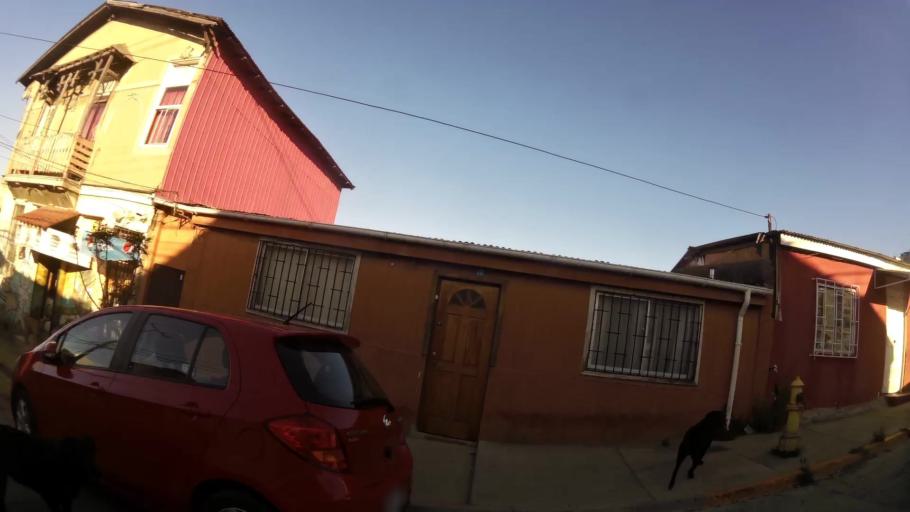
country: CL
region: Valparaiso
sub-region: Provincia de Valparaiso
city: Valparaiso
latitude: -33.0570
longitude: -71.6127
